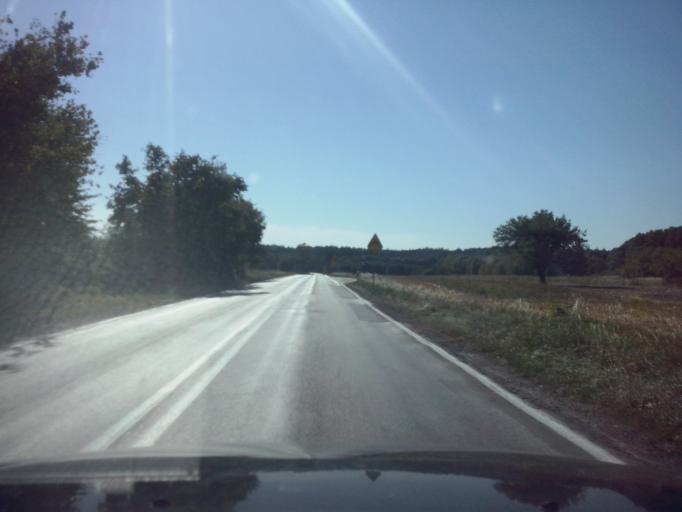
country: PL
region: Swietokrzyskie
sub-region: Powiat kielecki
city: Chmielnik
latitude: 50.6057
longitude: 20.6844
